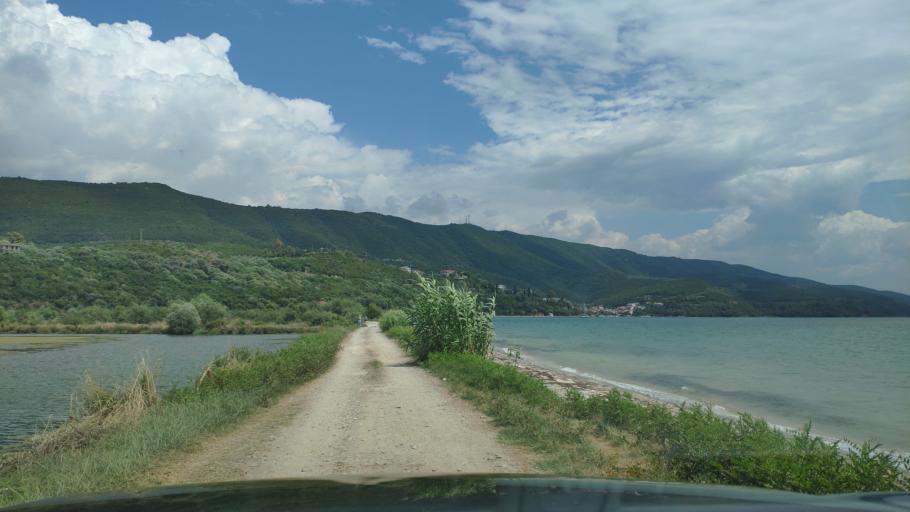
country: GR
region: West Greece
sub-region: Nomos Aitolias kai Akarnanias
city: Menidi
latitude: 39.0481
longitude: 21.1012
